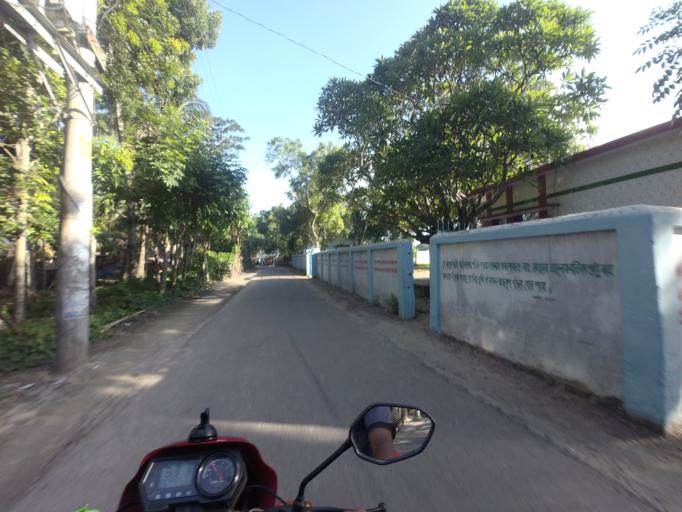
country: BD
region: Khulna
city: Khulna
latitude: 22.9160
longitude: 89.5188
